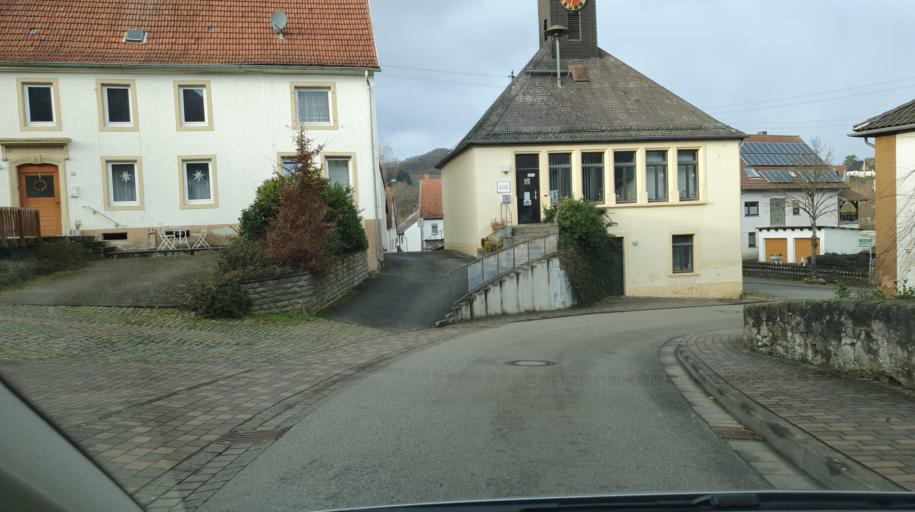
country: DE
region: Rheinland-Pfalz
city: Ulmet
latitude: 49.5856
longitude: 7.4553
